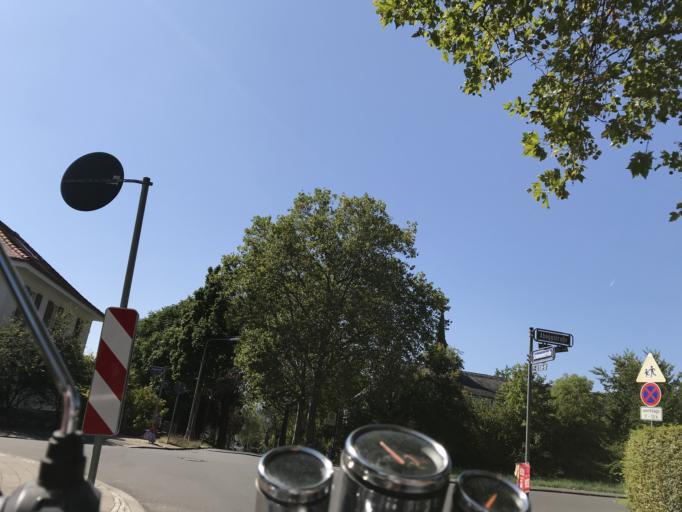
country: DE
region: Hesse
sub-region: Regierungsbezirk Darmstadt
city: Wiesbaden
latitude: 50.0907
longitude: 8.2514
